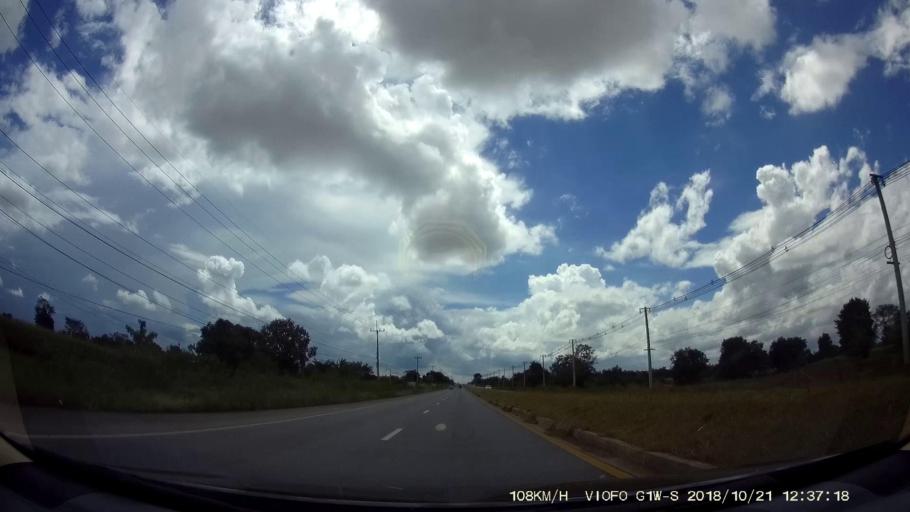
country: TH
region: Nakhon Ratchasima
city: Dan Khun Thot
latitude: 15.0712
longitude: 101.7122
